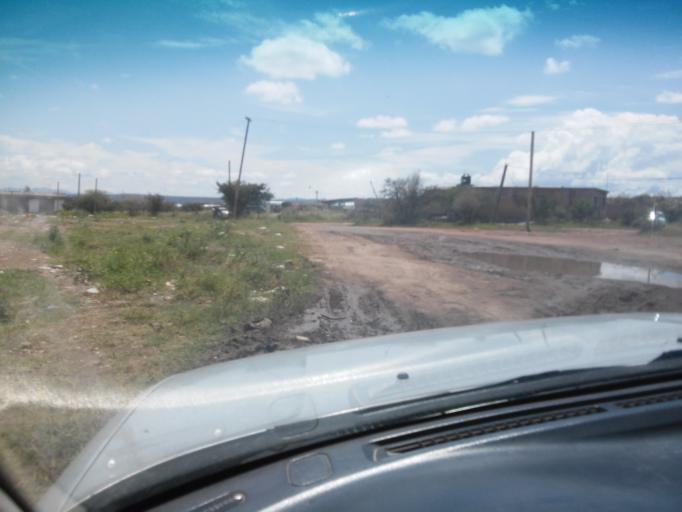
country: MX
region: Durango
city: Victoria de Durango
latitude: 23.9844
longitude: -104.7096
